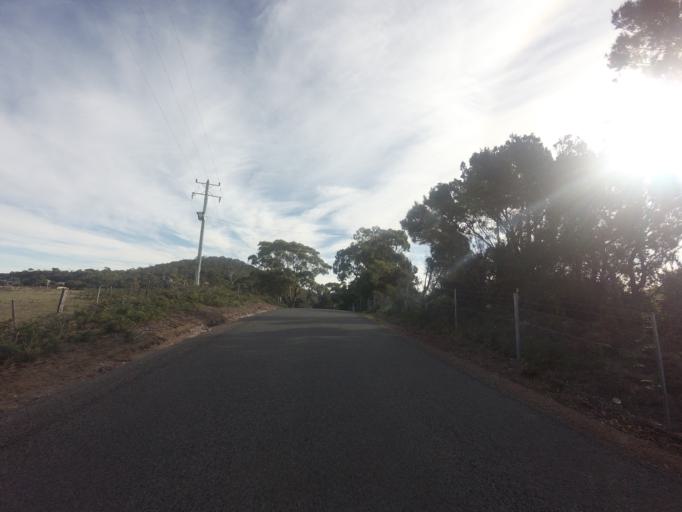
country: AU
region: Tasmania
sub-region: Sorell
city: Sorell
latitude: -42.9638
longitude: 147.8337
